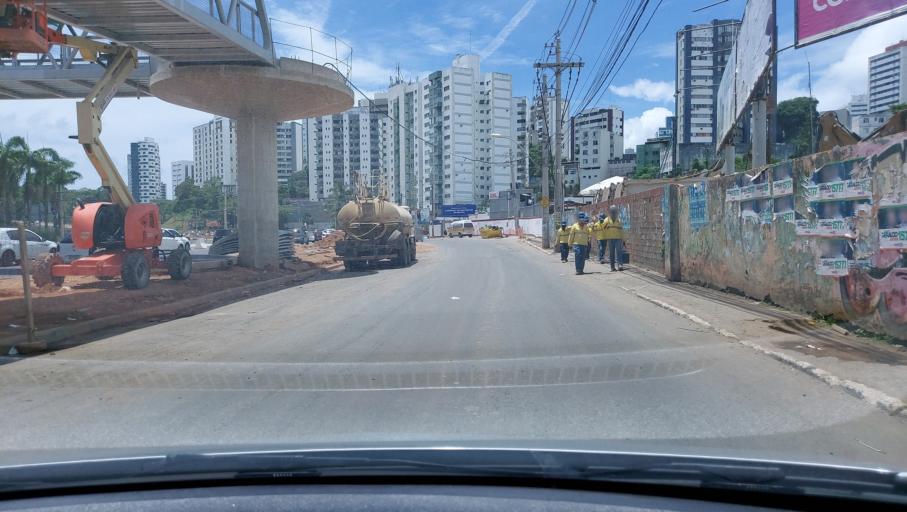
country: BR
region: Bahia
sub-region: Salvador
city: Salvador
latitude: -12.9914
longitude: -38.4750
